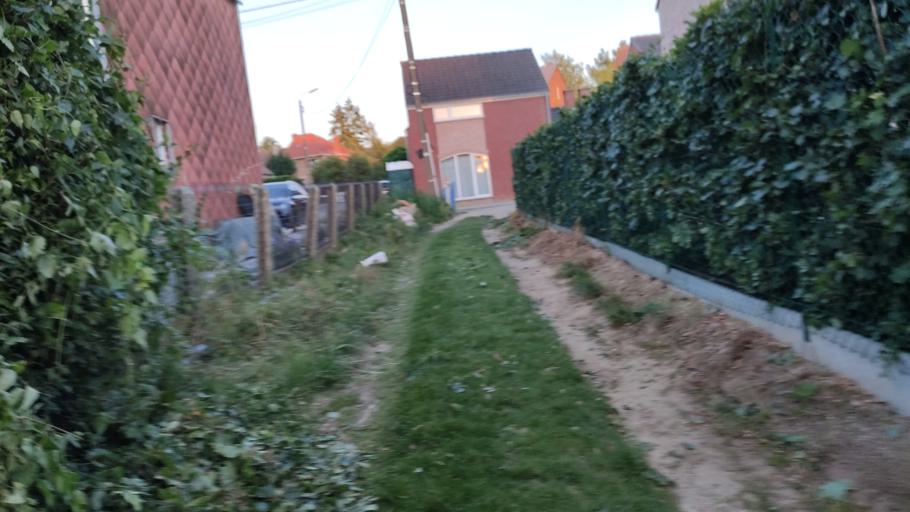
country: BE
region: Flanders
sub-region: Provincie Vlaams-Brabant
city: Hoegaarden
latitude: 50.7597
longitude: 4.8877
